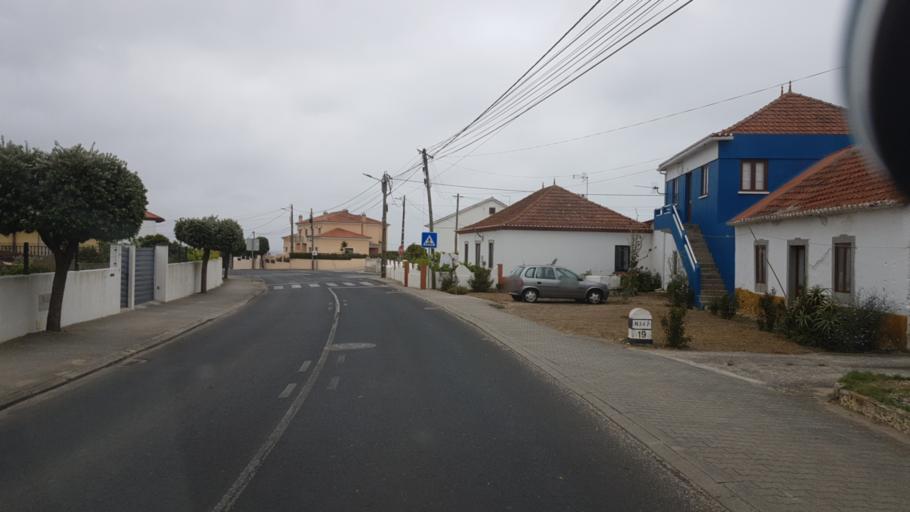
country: PT
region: Lisbon
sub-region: Lourinha
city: Lourinha
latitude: 39.1970
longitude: -9.3350
